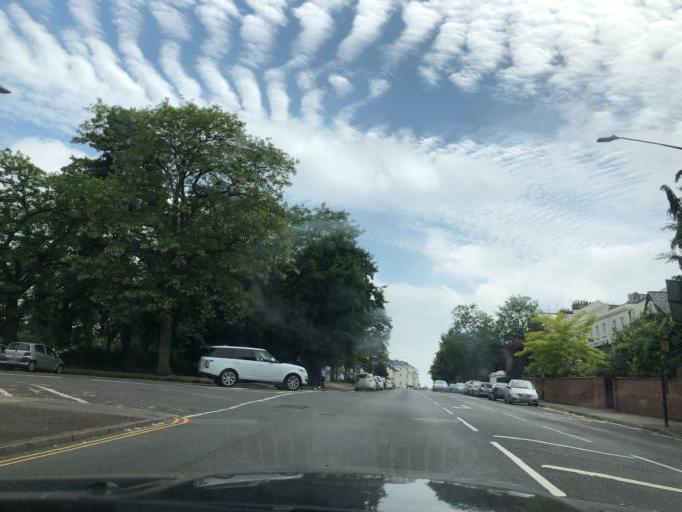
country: GB
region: England
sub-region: Warwickshire
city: Royal Leamington Spa
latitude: 52.2950
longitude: -1.5400
